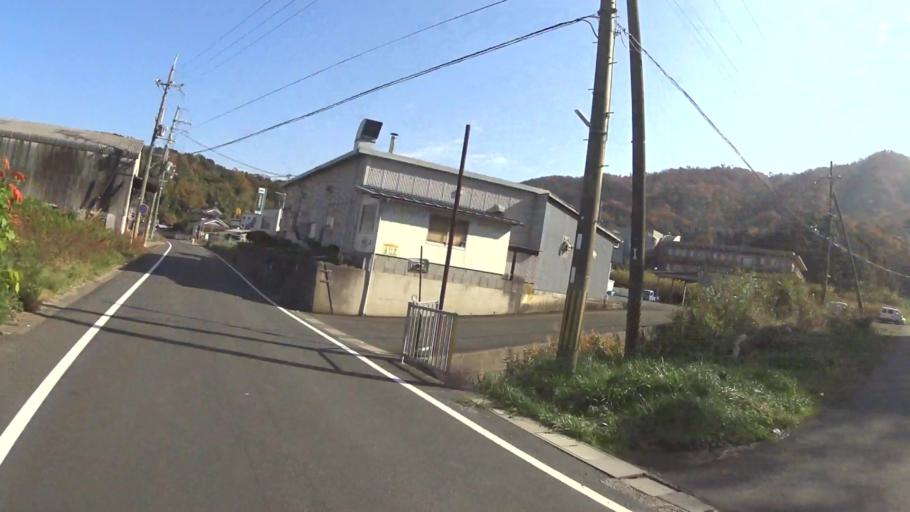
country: JP
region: Kyoto
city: Maizuru
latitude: 35.4730
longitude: 135.3397
